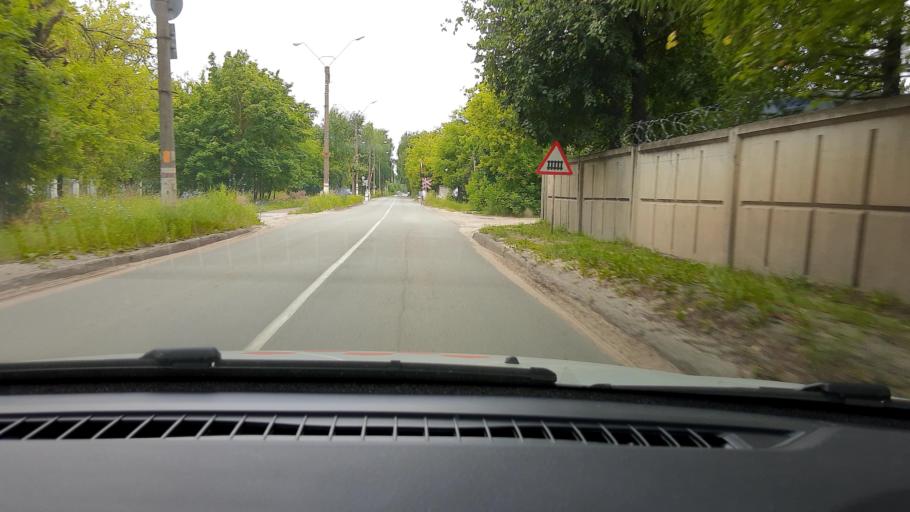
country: RU
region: Nizjnij Novgorod
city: Pyra
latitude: 56.2524
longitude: 43.3951
